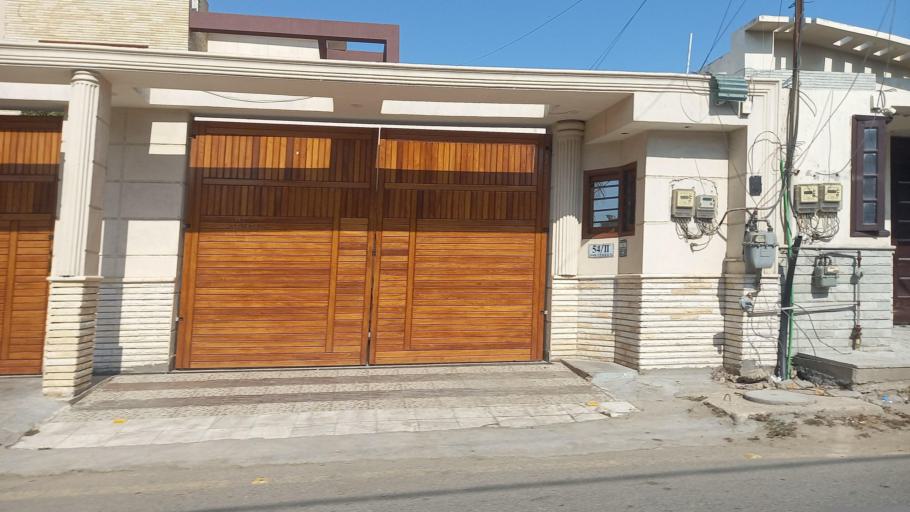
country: PK
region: Sindh
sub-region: Karachi District
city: Karachi
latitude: 24.8013
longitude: 67.0457
